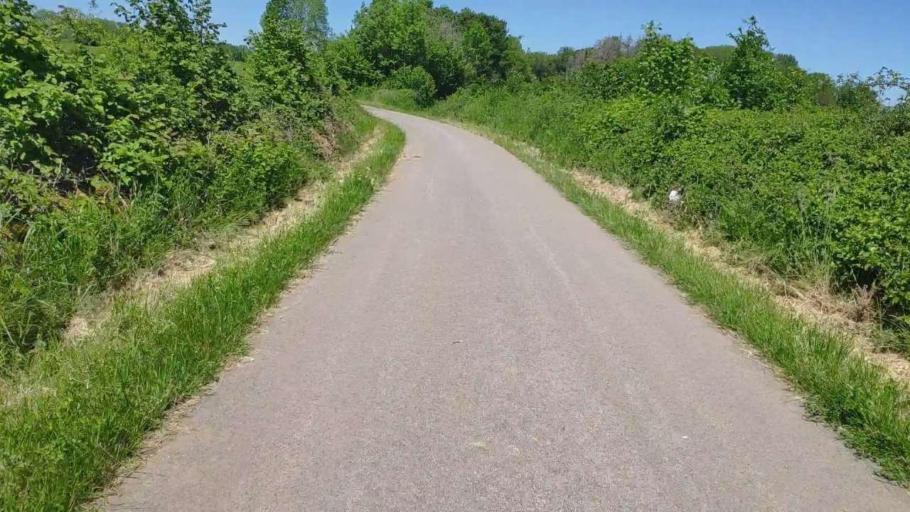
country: FR
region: Franche-Comte
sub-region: Departement du Jura
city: Perrigny
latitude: 46.7184
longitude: 5.6668
